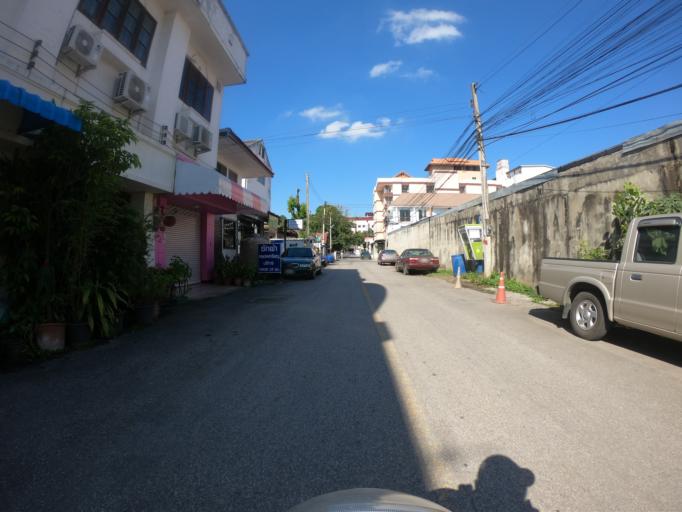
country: TH
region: Chiang Mai
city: Chiang Mai
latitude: 18.8020
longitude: 98.9751
